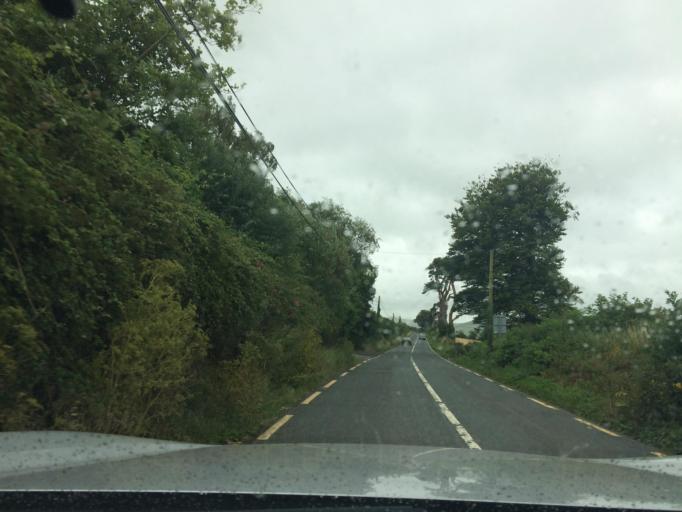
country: IE
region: Munster
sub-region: South Tipperary
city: Cluain Meala
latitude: 52.2988
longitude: -7.7876
